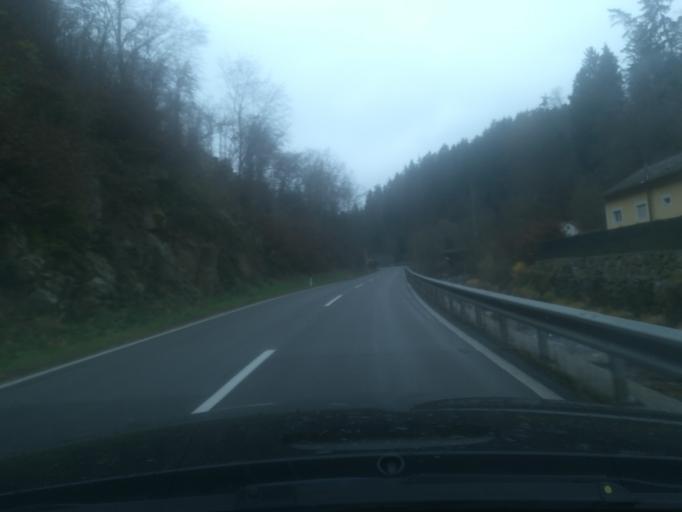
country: AT
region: Upper Austria
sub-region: Politischer Bezirk Perg
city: Perg
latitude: 48.3260
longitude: 14.5658
